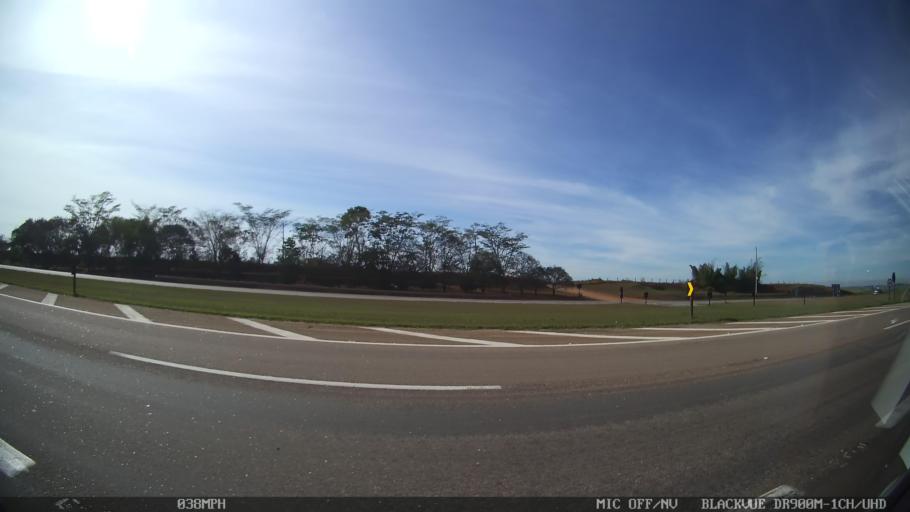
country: BR
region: Sao Paulo
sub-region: Rio Das Pedras
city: Rio das Pedras
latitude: -22.7928
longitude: -47.5820
